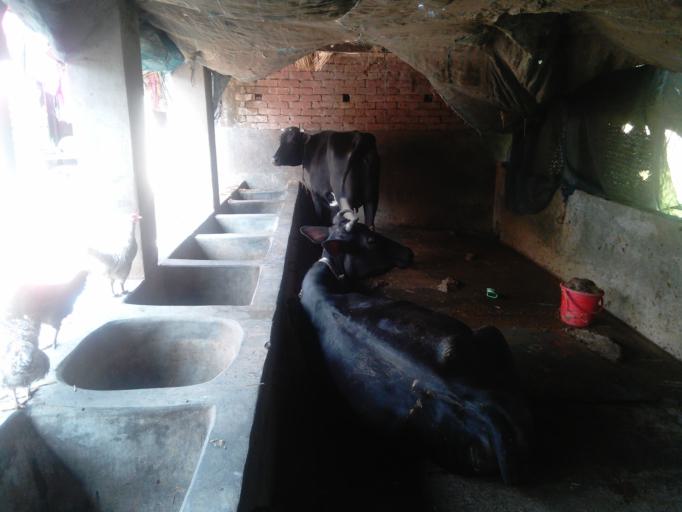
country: BD
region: Khulna
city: Kesabpur
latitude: 22.7862
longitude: 89.2786
